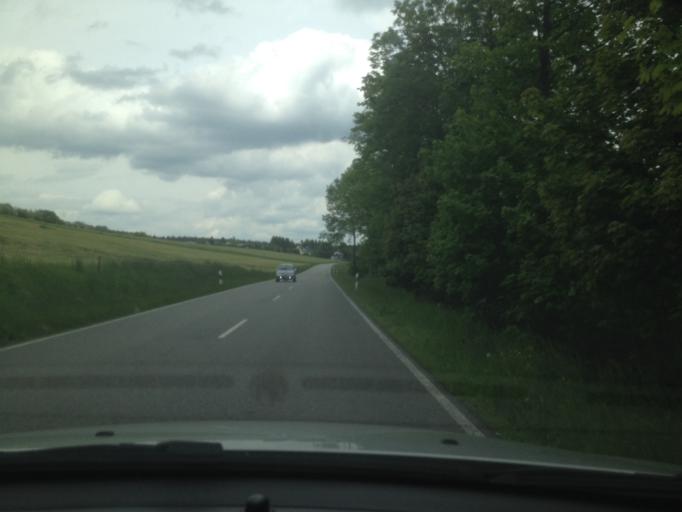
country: DE
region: Saxony
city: Lossnitz
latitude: 50.6501
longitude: 12.7591
